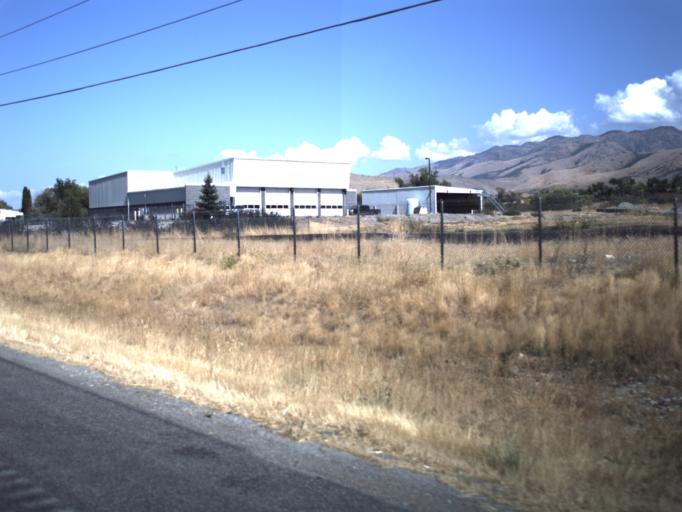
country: US
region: Utah
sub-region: Cache County
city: Richmond
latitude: 41.9397
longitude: -111.8138
